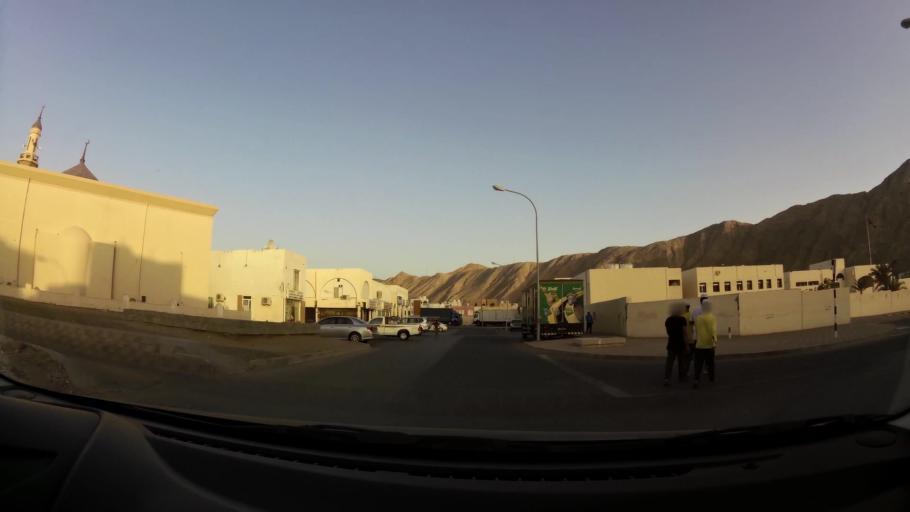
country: OM
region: Muhafazat Masqat
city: Muscat
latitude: 23.5748
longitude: 58.5697
